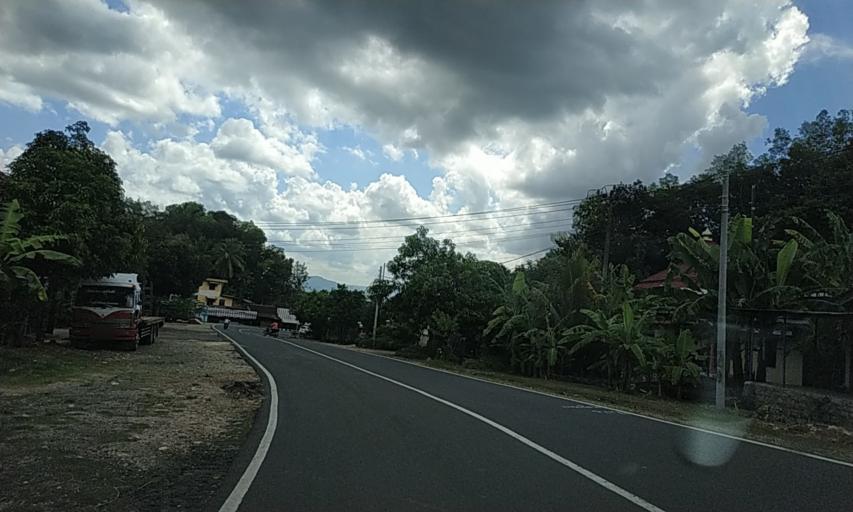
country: ID
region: East Java
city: Krajan
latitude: -8.0317
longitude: 110.9398
